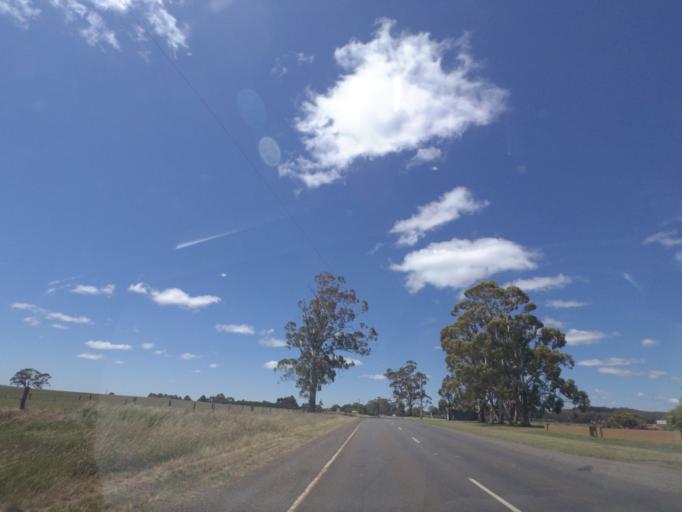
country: AU
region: Victoria
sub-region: Mount Alexander
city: Castlemaine
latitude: -37.3079
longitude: 144.2316
